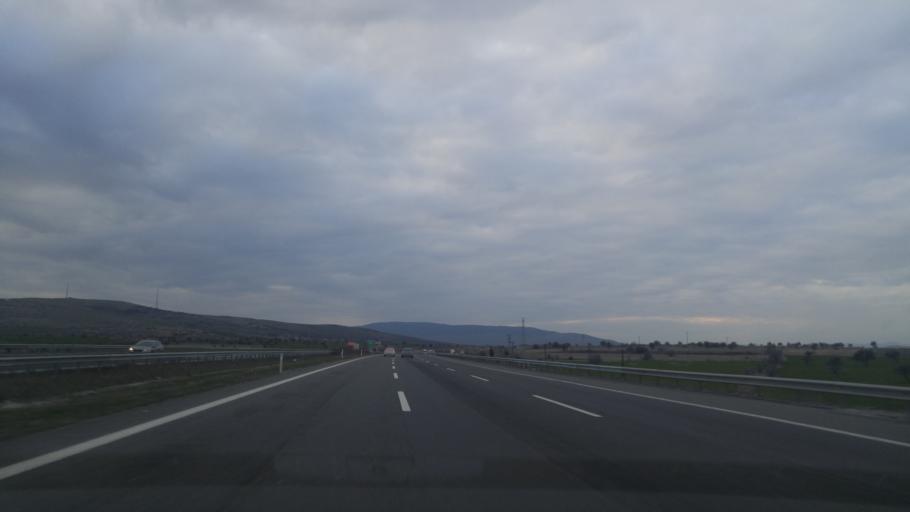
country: TR
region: Ankara
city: Celtikci
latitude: 40.2516
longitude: 32.4855
